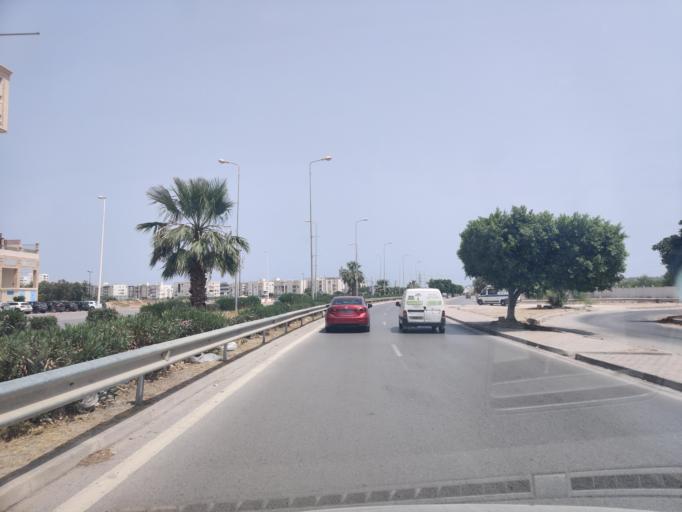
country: TN
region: Tunis
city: La Goulette
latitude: 36.8419
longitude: 10.2974
